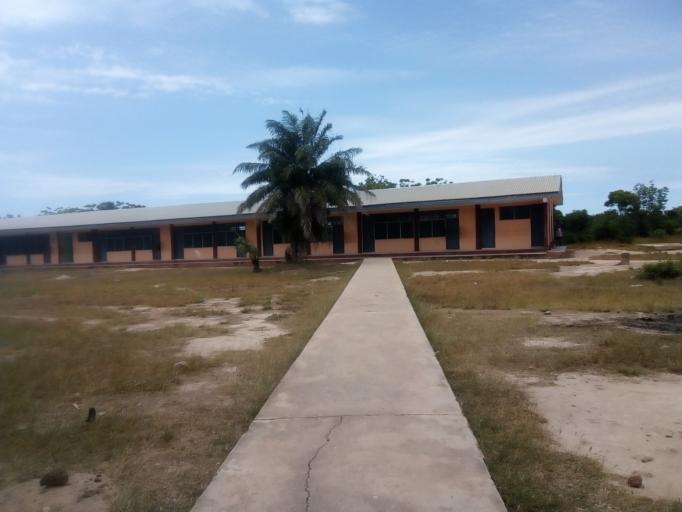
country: GH
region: Volta
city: Anloga
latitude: 5.8005
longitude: 0.6151
